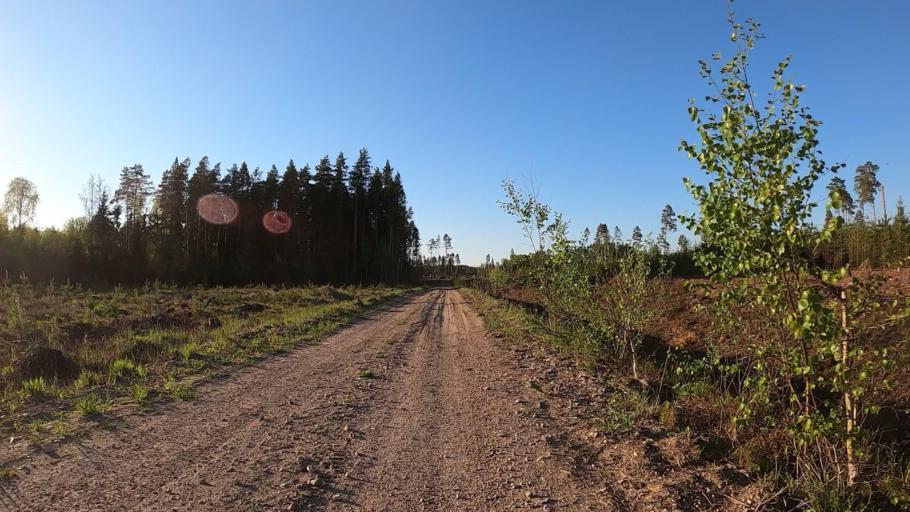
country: LV
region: Kekava
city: Kekava
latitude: 56.7721
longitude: 24.2227
